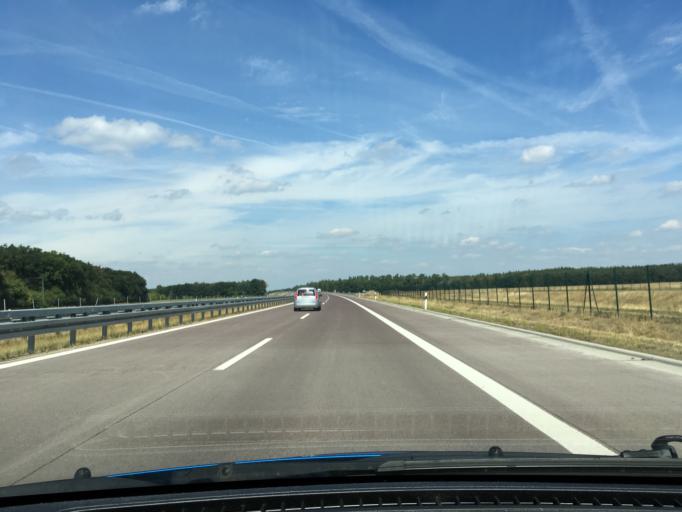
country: DE
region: Mecklenburg-Vorpommern
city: Gross Laasch
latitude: 53.3273
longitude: 11.5275
